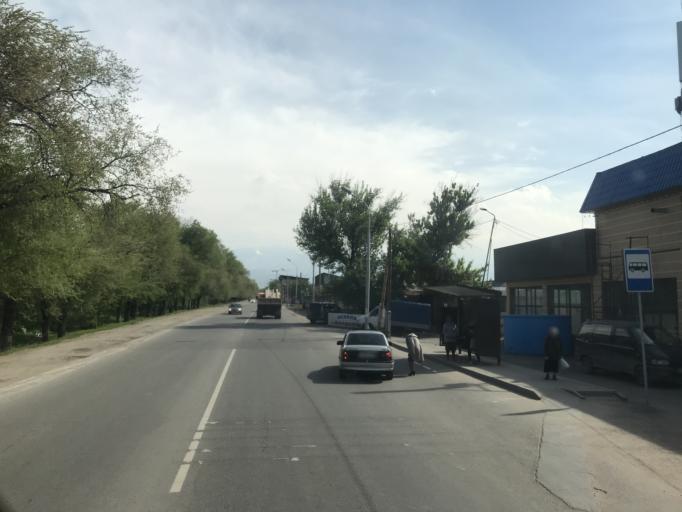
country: KZ
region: Almaty Oblysy
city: Burunday
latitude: 43.2475
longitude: 76.8038
